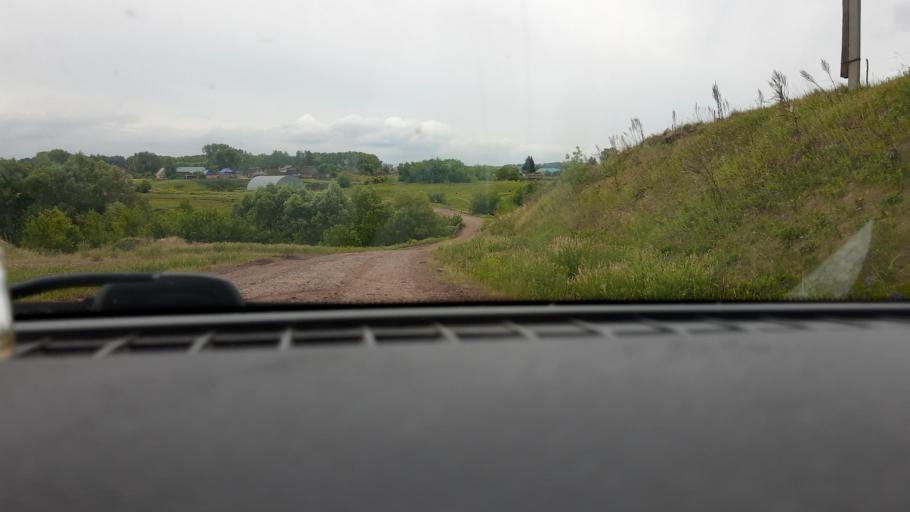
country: RU
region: Bashkortostan
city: Chishmy
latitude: 54.6832
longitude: 55.4831
